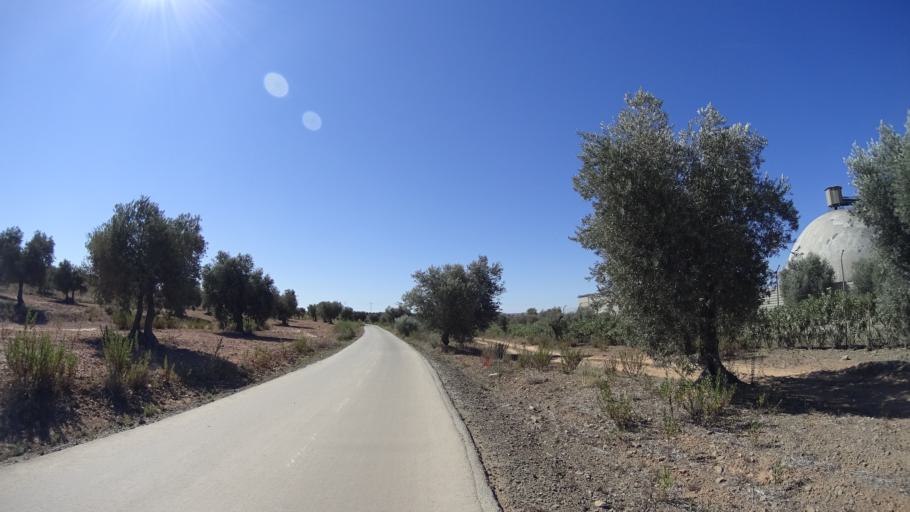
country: ES
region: Madrid
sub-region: Provincia de Madrid
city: Morata de Tajuna
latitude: 40.2454
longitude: -3.4702
